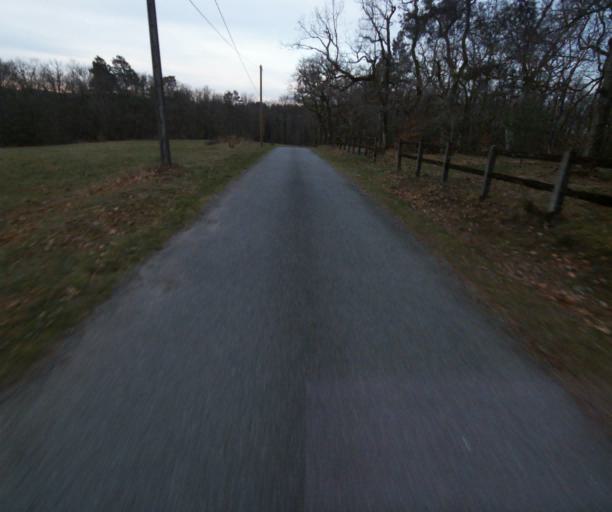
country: FR
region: Limousin
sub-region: Departement de la Correze
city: Correze
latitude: 45.4355
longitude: 1.8419
